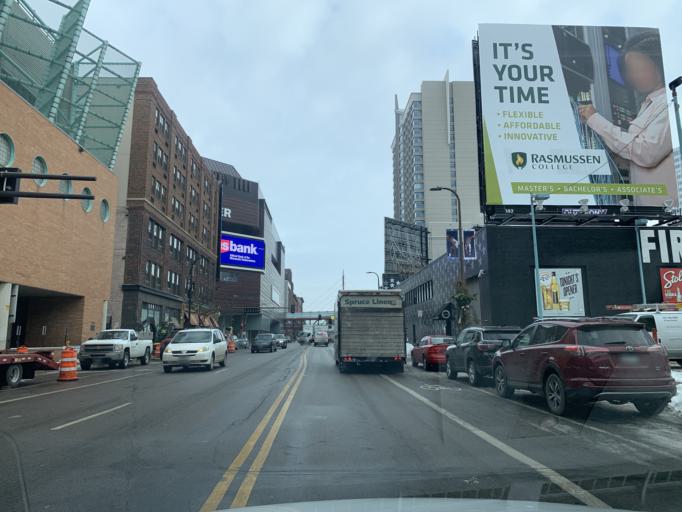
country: US
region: Minnesota
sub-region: Hennepin County
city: Minneapolis
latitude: 44.9781
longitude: -93.2769
